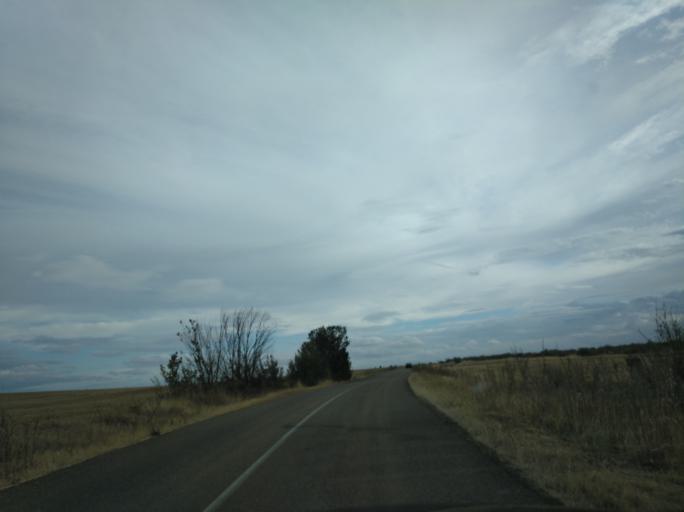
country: ES
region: Extremadura
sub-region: Provincia de Badajoz
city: Badajoz
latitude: 38.9000
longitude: -7.0165
